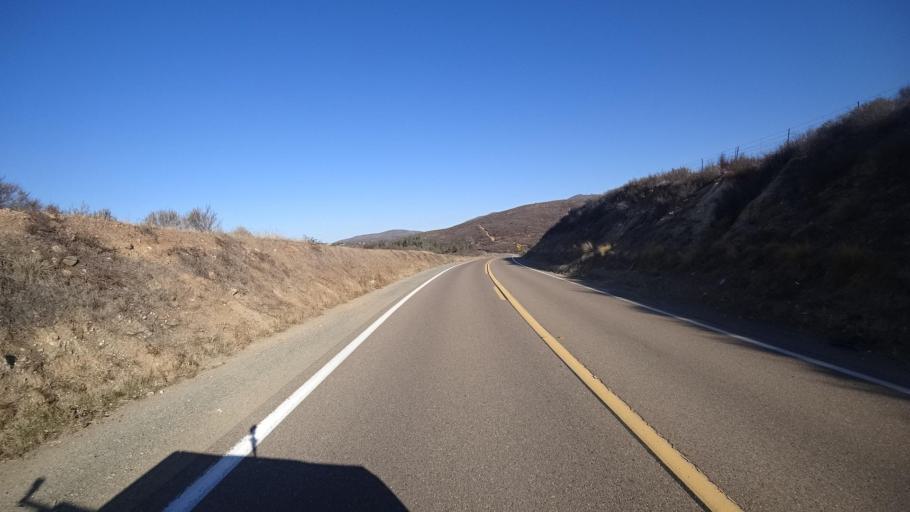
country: US
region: California
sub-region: San Diego County
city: Jamul
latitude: 32.6454
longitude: -116.9270
